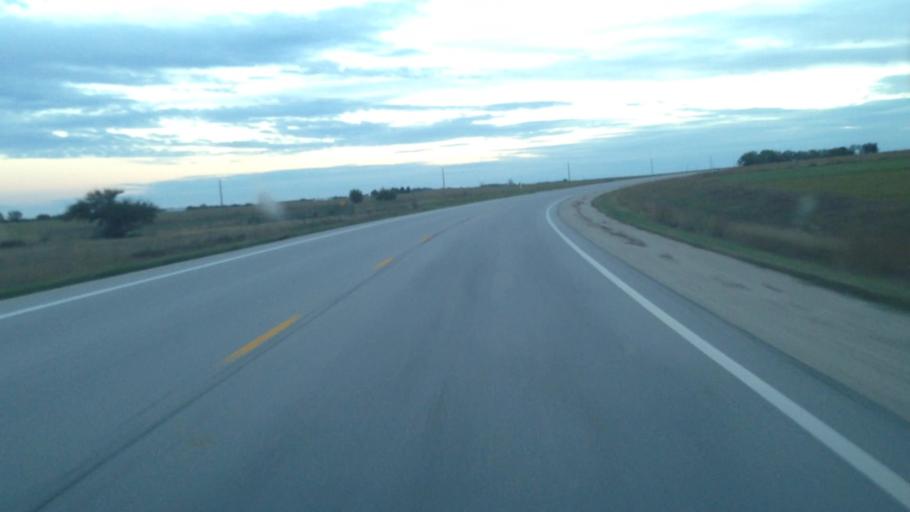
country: US
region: Kansas
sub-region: Anderson County
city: Garnett
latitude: 38.1926
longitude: -95.2425
